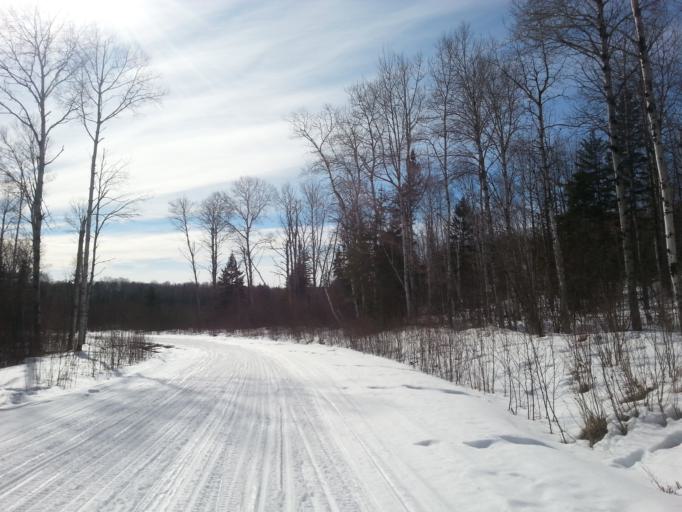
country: CA
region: Ontario
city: Greater Sudbury
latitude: 46.3301
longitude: -80.9067
